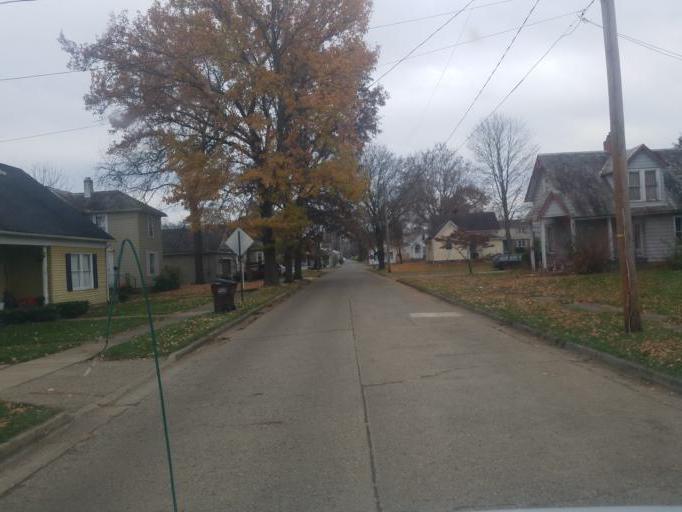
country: US
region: Ohio
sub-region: Knox County
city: Mount Vernon
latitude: 40.3948
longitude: -82.4726
